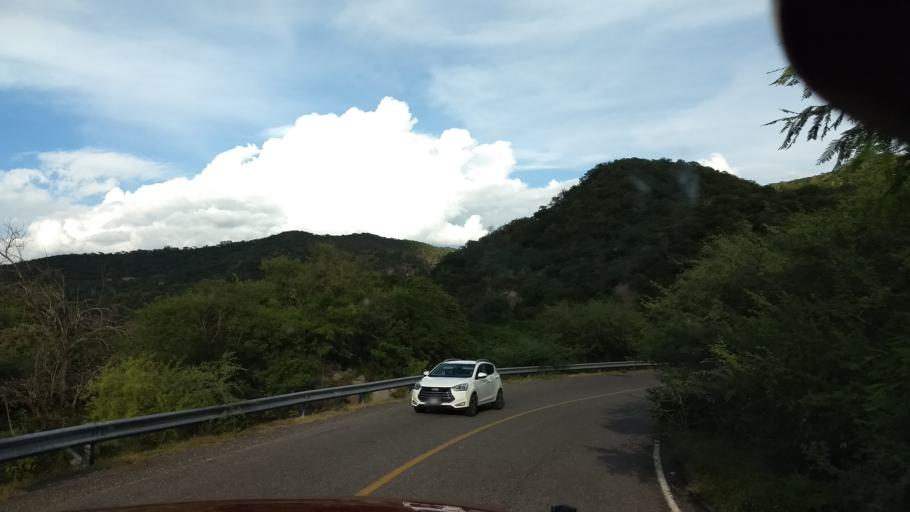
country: MX
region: Colima
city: Suchitlan
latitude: 19.4606
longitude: -103.8272
